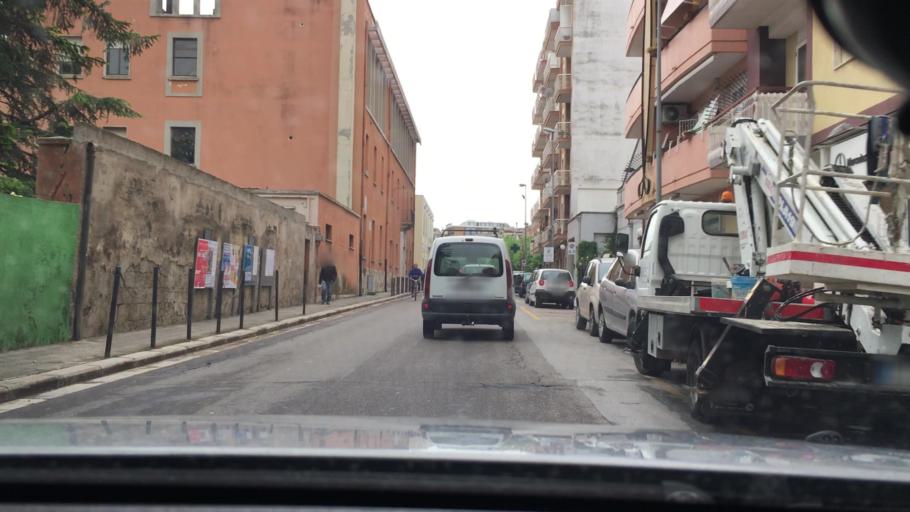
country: IT
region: Apulia
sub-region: Provincia di Bari
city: Gioia del Colle
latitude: 40.8047
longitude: 16.9237
